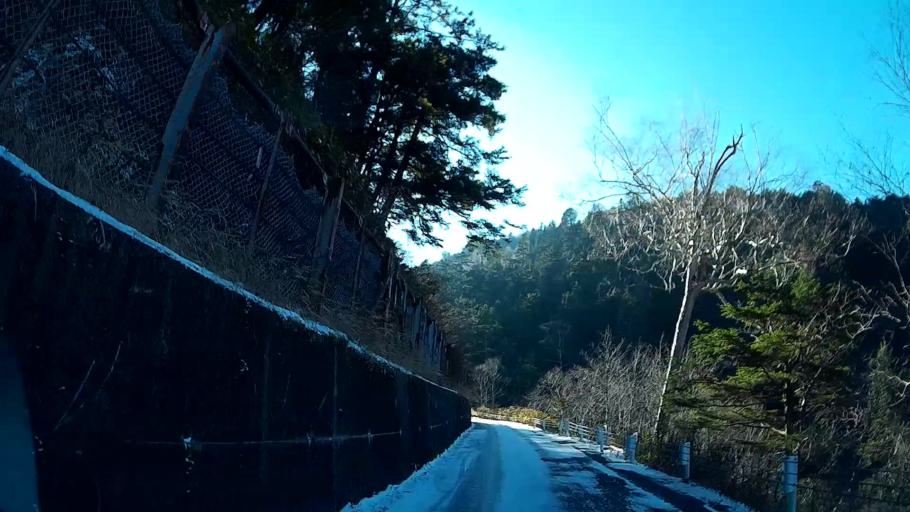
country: JP
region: Nagano
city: Hotaka
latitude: 36.2024
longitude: 137.5903
